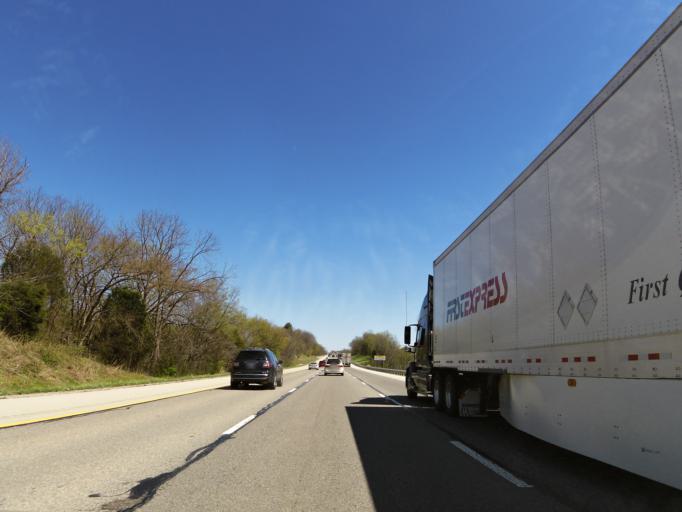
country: US
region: Kentucky
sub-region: Edmonson County
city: Brownsville
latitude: 37.0178
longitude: -86.2691
